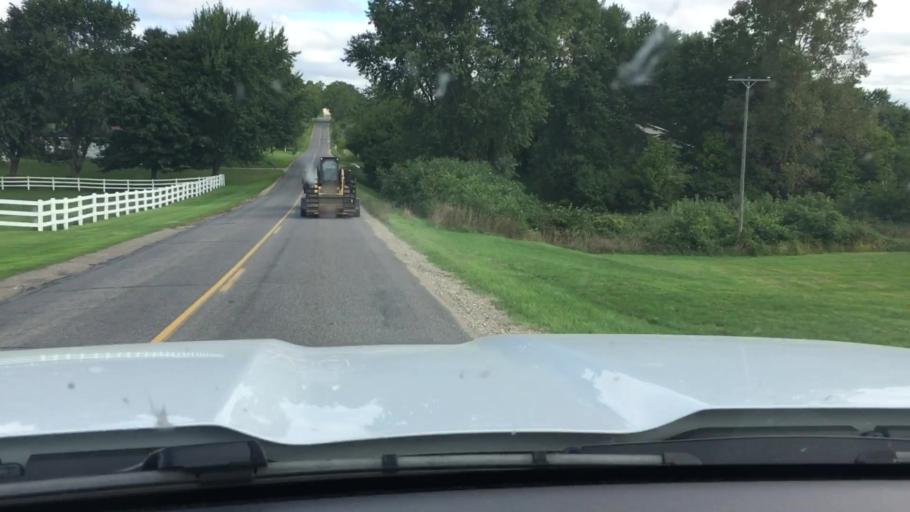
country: US
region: Michigan
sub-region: Kent County
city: Byron Center
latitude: 42.8048
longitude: -85.8026
